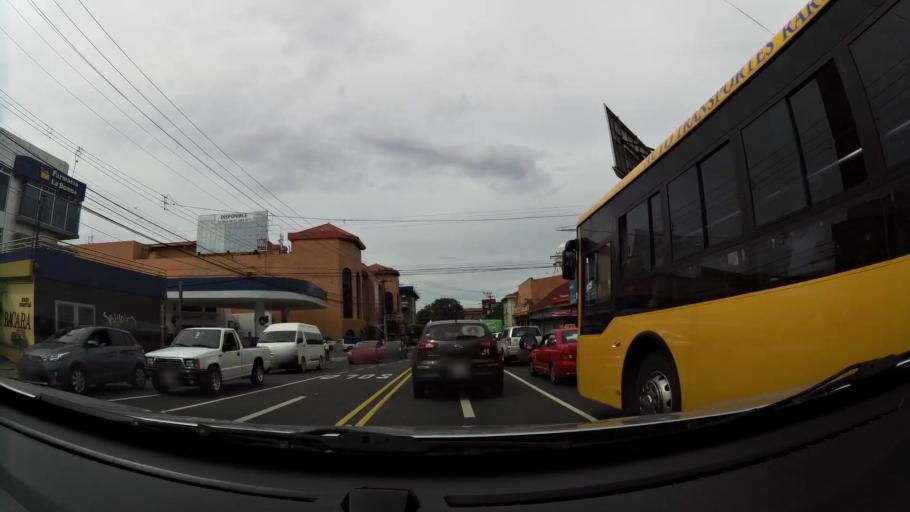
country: CR
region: San Jose
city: San Pedro
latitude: 9.9320
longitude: -84.0516
